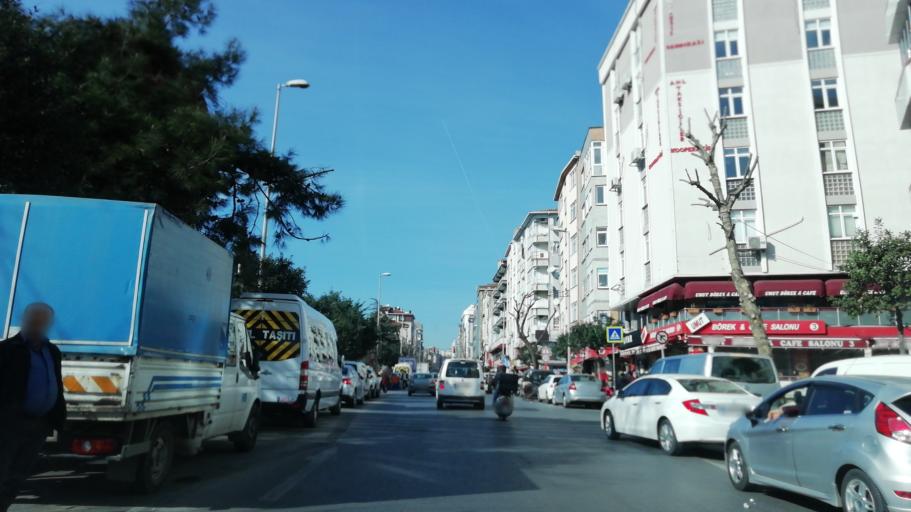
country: TR
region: Istanbul
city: Bahcelievler
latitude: 40.9954
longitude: 28.8350
